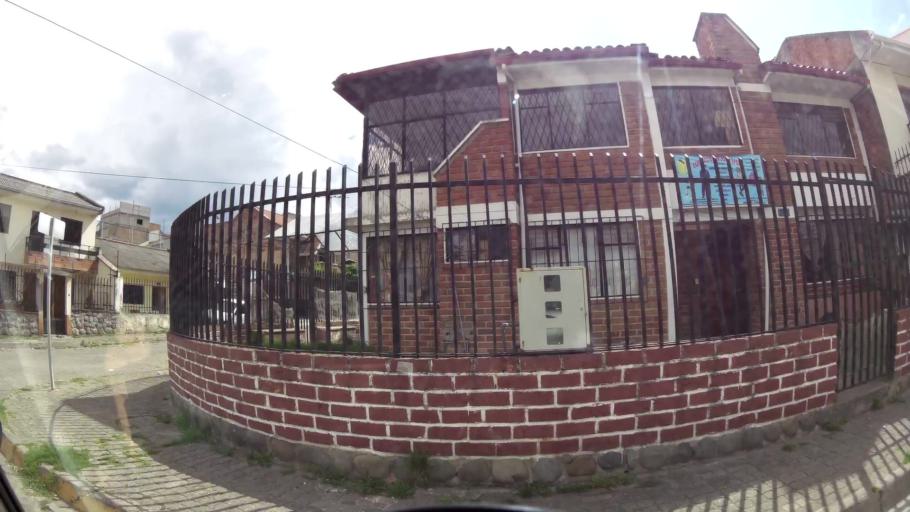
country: EC
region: Azuay
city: Cuenca
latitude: -2.8827
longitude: -78.9812
